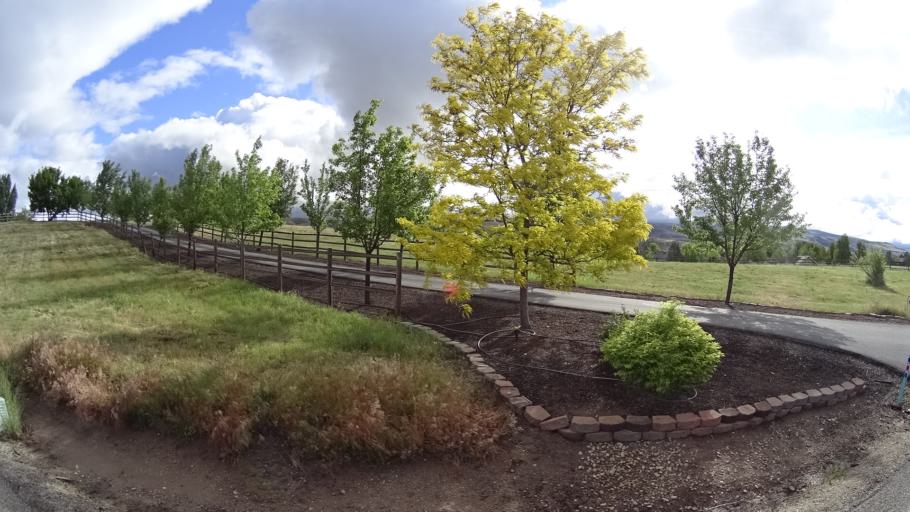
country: US
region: Idaho
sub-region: Ada County
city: Eagle
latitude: 43.7263
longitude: -116.2638
